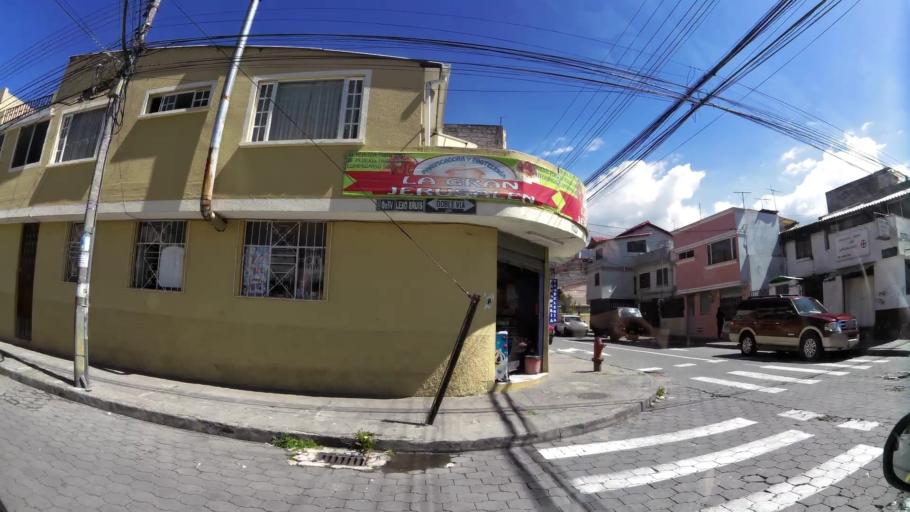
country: EC
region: Pichincha
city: Quito
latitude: -0.2536
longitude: -78.5370
